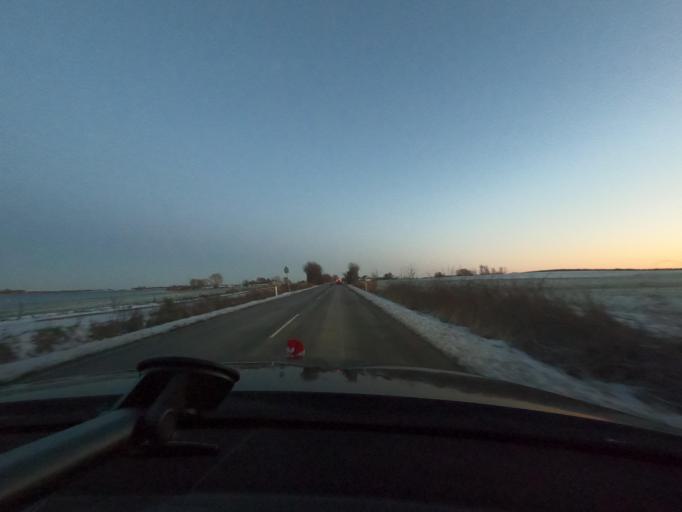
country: DK
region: South Denmark
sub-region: Sonderborg Kommune
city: Horuphav
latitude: 54.8683
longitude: 9.9525
